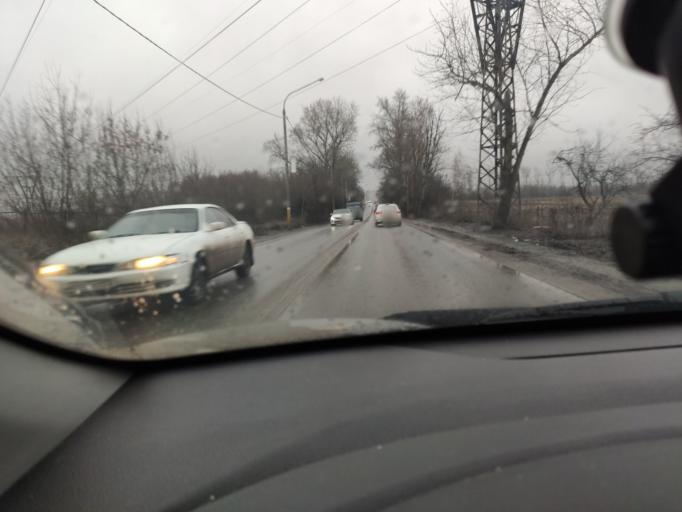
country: RU
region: Moskovskaya
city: Biryulevo Zapadnoye
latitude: 55.5669
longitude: 37.6470
